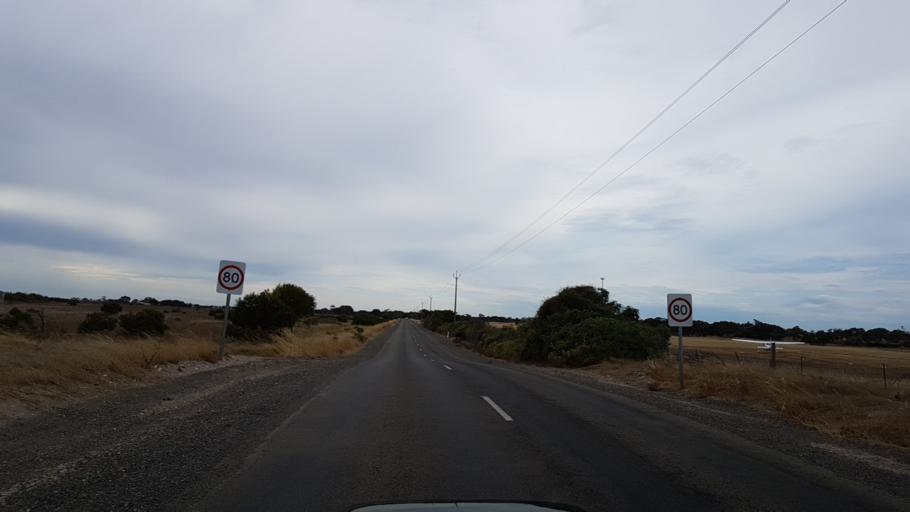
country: AU
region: South Australia
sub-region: Yorke Peninsula
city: Port Victoria
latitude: -34.9175
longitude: 137.0654
